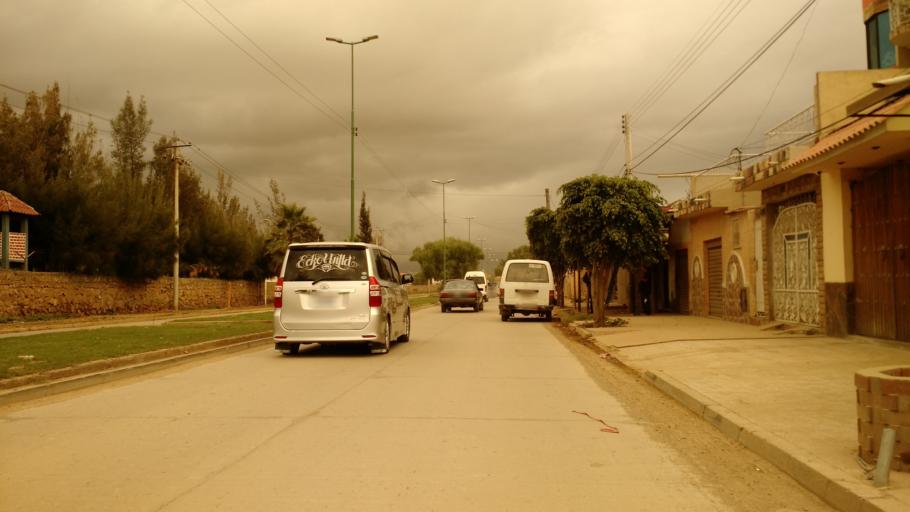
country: BO
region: Cochabamba
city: Cochabamba
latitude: -17.4259
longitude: -66.1662
